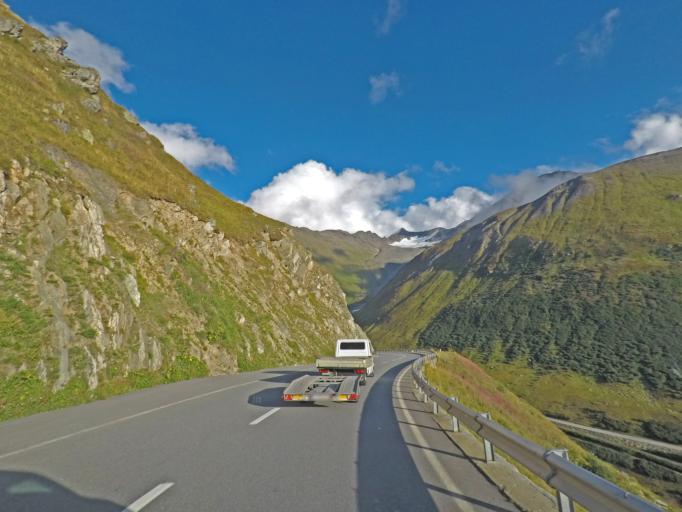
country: IT
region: Piedmont
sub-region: Provincia Verbano-Cusio-Ossola
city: Formazza
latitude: 46.5741
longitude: 8.3893
